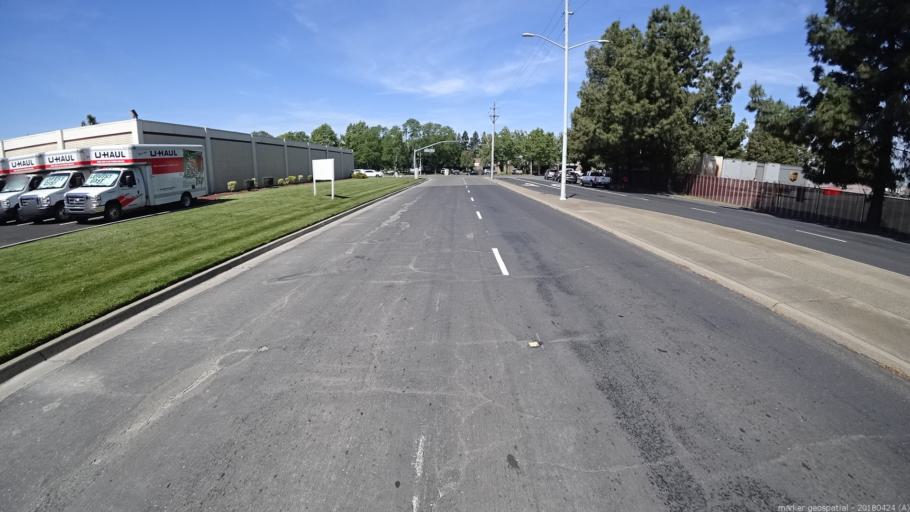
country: US
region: California
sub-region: Yolo County
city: West Sacramento
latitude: 38.5699
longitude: -121.5481
